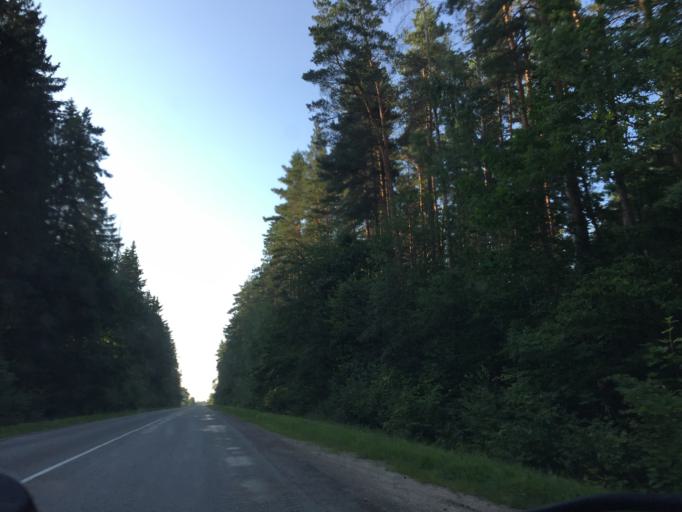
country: LV
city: Tervete
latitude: 56.4630
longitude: 23.4041
